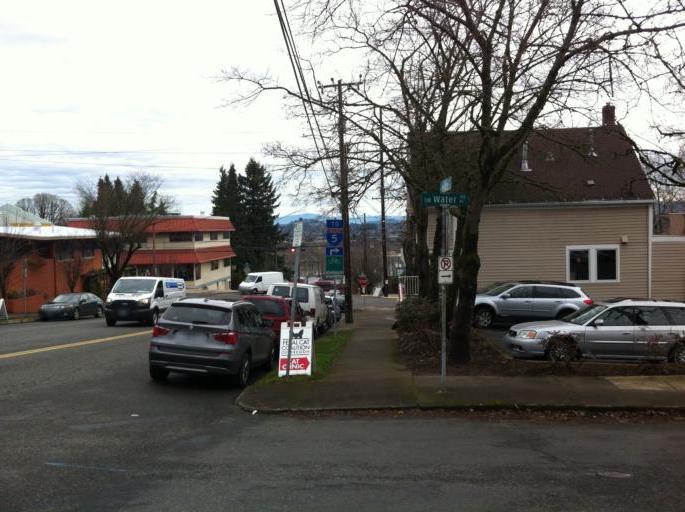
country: US
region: Oregon
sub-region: Multnomah County
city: Portland
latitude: 45.4908
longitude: -122.6771
